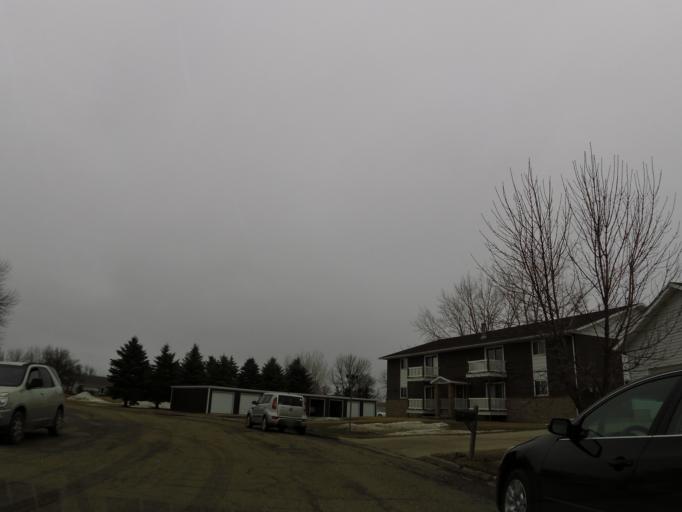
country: US
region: North Dakota
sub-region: Walsh County
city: Grafton
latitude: 48.4057
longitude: -97.4100
